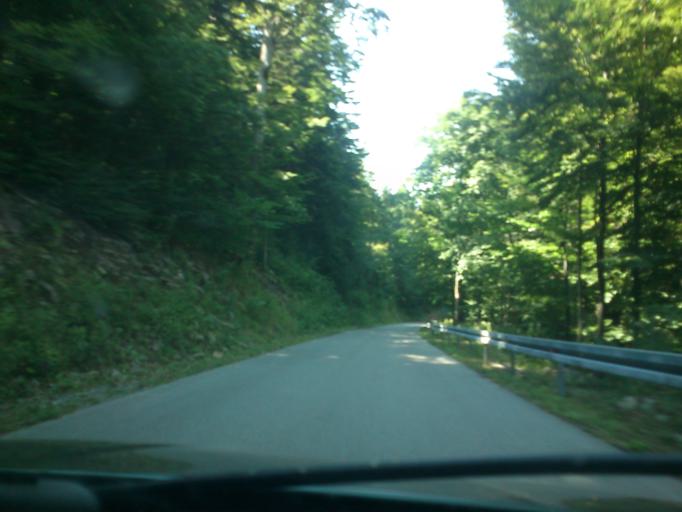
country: HR
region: Licko-Senjska
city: Senj
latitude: 44.8408
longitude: 15.0000
